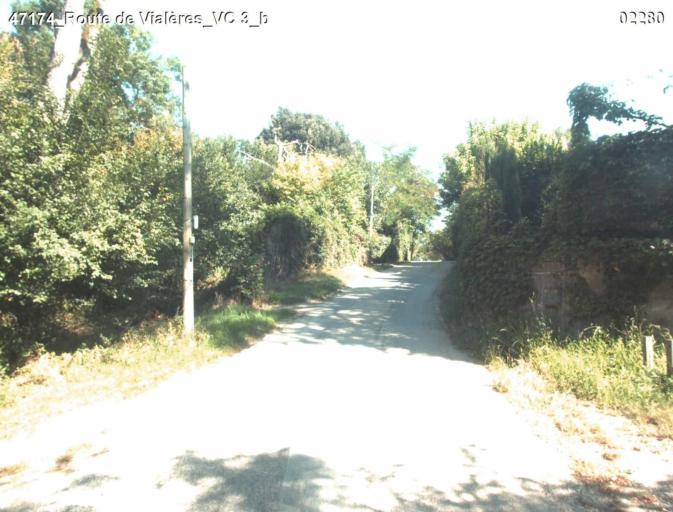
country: FR
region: Aquitaine
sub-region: Departement du Lot-et-Garonne
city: Nerac
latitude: 44.0533
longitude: 0.3830
